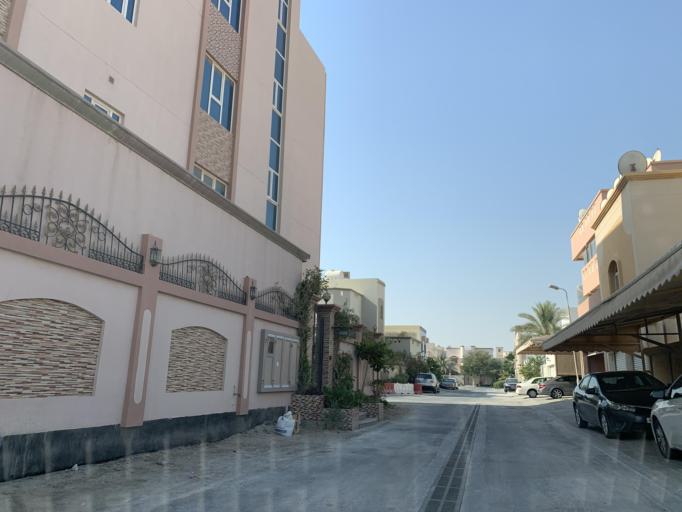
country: BH
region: Manama
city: Jidd Hafs
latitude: 26.1982
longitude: 50.5156
